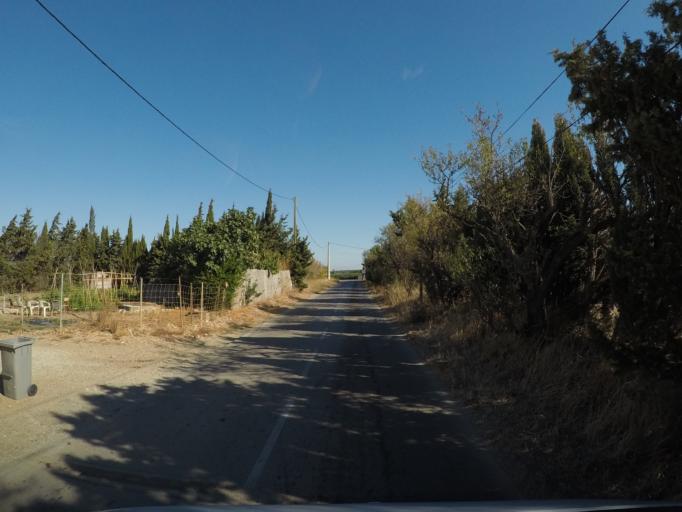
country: FR
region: Languedoc-Roussillon
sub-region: Departement de l'Aude
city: Narbonne
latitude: 43.1602
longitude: 3.0117
